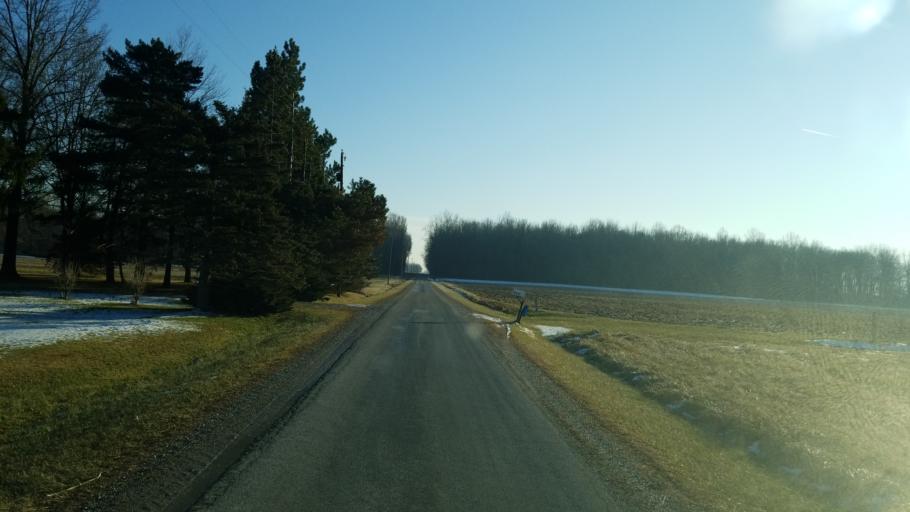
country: US
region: Ohio
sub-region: Crawford County
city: Bucyrus
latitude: 40.9295
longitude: -82.9211
